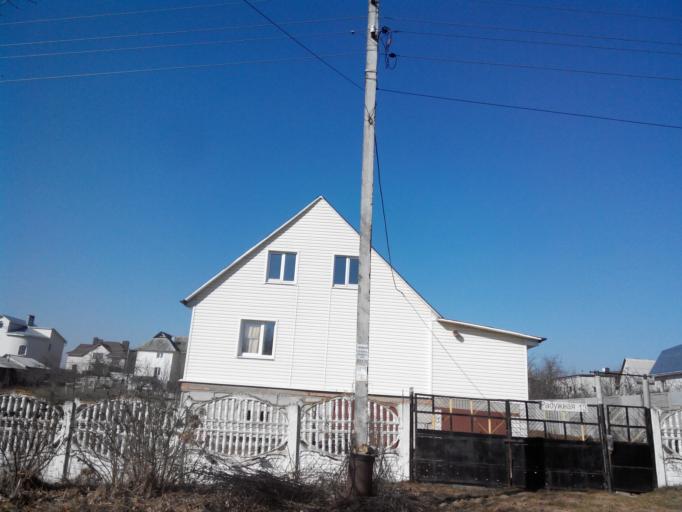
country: BY
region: Minsk
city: Zhdanovichy
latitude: 53.9229
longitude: 27.4022
